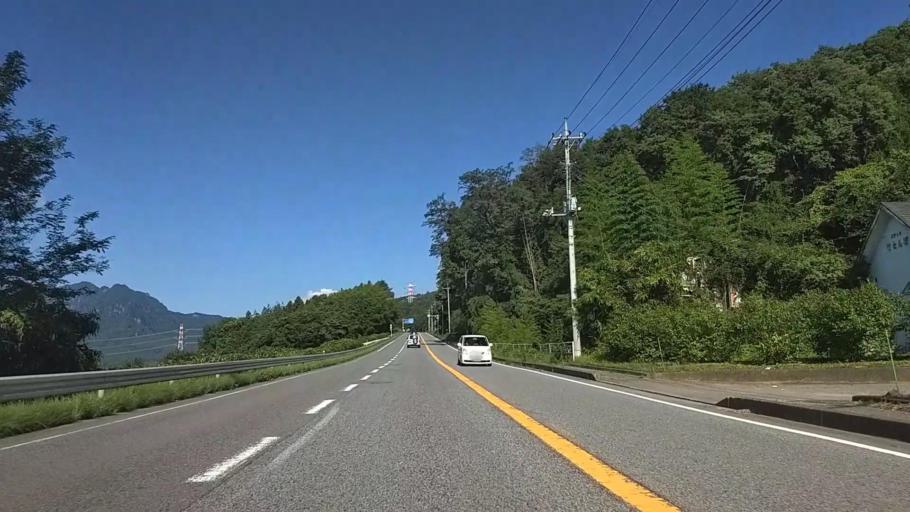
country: JP
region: Gunma
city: Annaka
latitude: 36.3182
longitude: 138.7958
